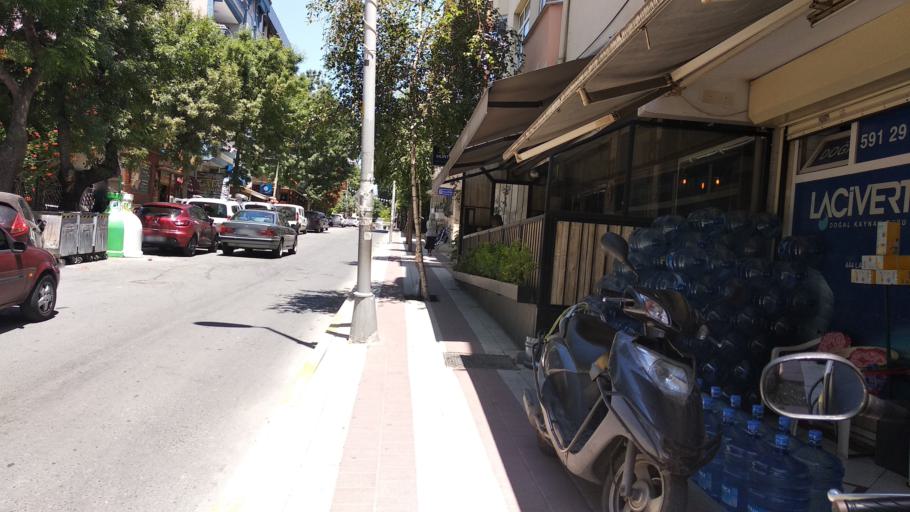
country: TR
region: Istanbul
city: Yakuplu
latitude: 40.9753
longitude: 28.7203
